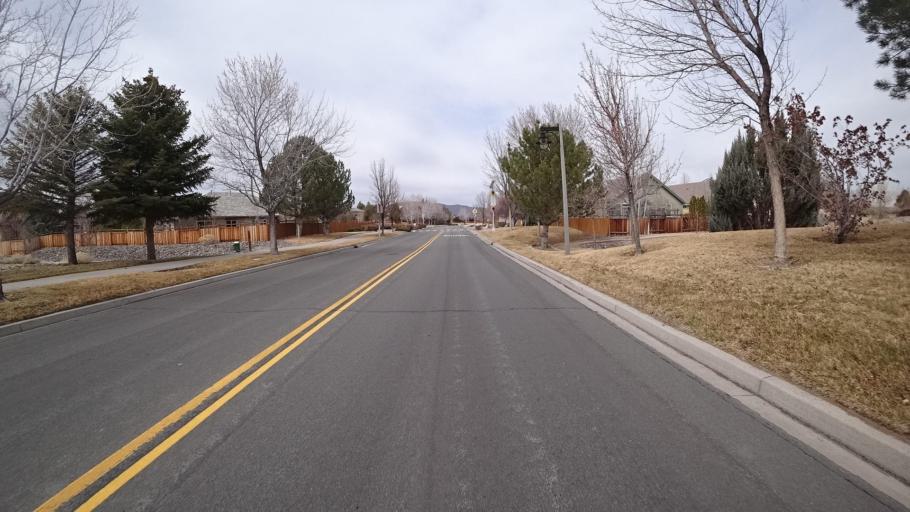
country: US
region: Nevada
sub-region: Washoe County
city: Spanish Springs
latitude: 39.6213
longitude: -119.6820
